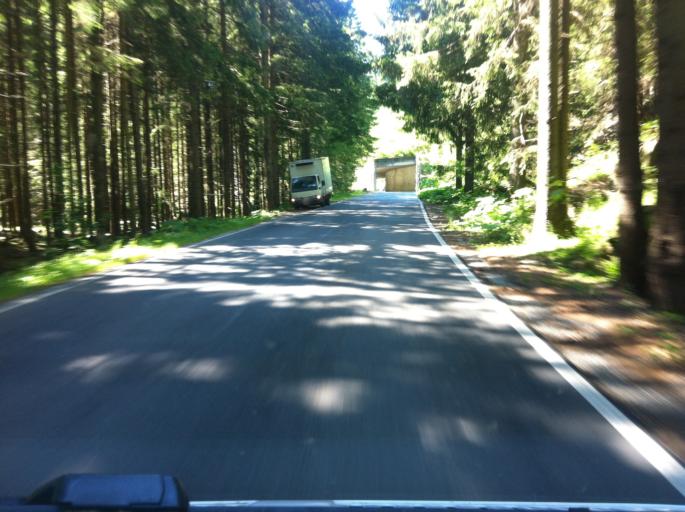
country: IT
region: Lombardy
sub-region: Provincia di Sondrio
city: Campodolcino
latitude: 46.4278
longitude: 9.3397
